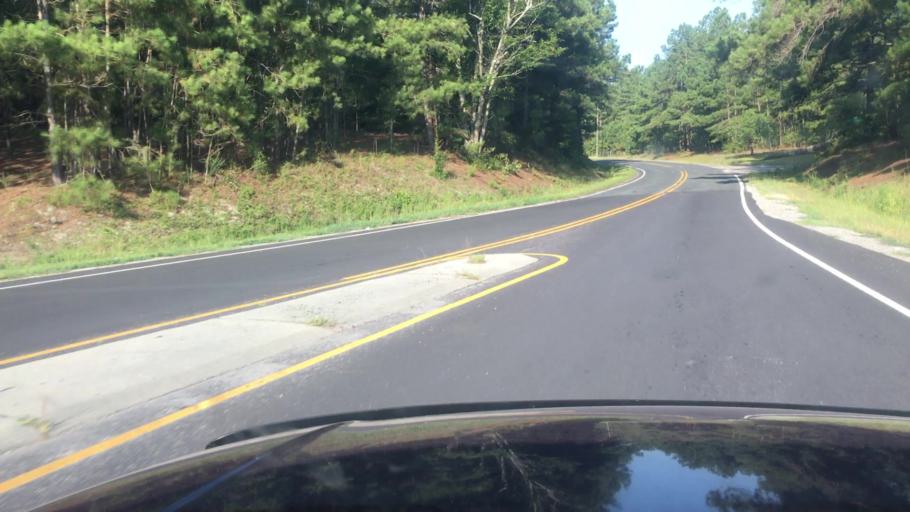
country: US
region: North Carolina
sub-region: Robeson County
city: Saint Pauls
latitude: 34.8548
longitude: -78.8506
